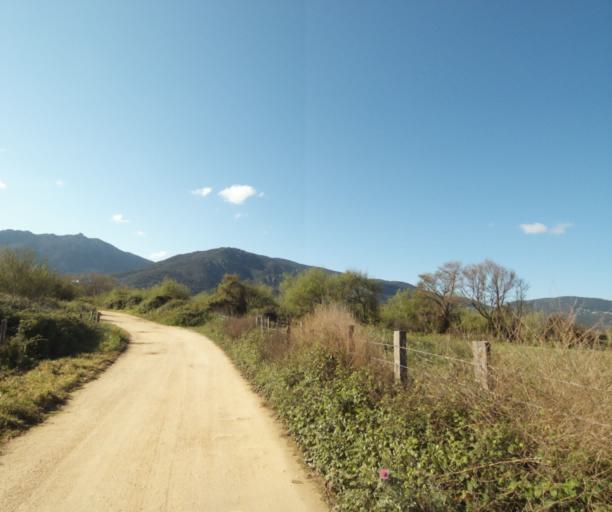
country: FR
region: Corsica
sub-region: Departement de la Corse-du-Sud
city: Propriano
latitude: 41.6644
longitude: 8.8928
